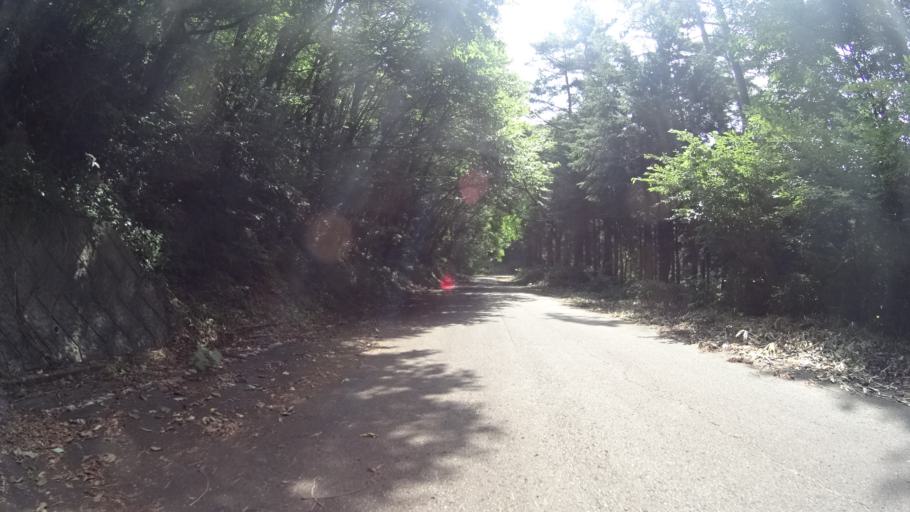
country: JP
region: Yamanashi
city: Nirasaki
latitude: 35.8853
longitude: 138.4774
